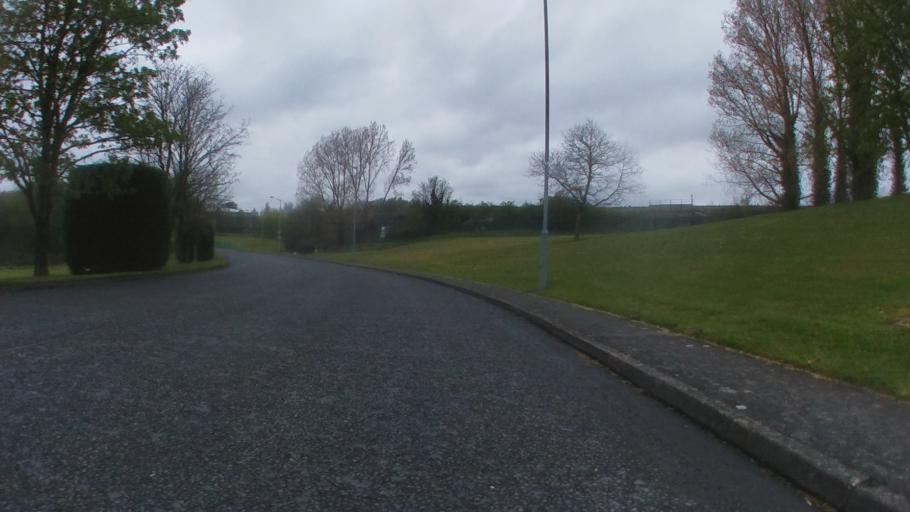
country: IE
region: Leinster
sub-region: Kilkenny
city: Kilkenny
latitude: 52.6474
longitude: -7.2169
